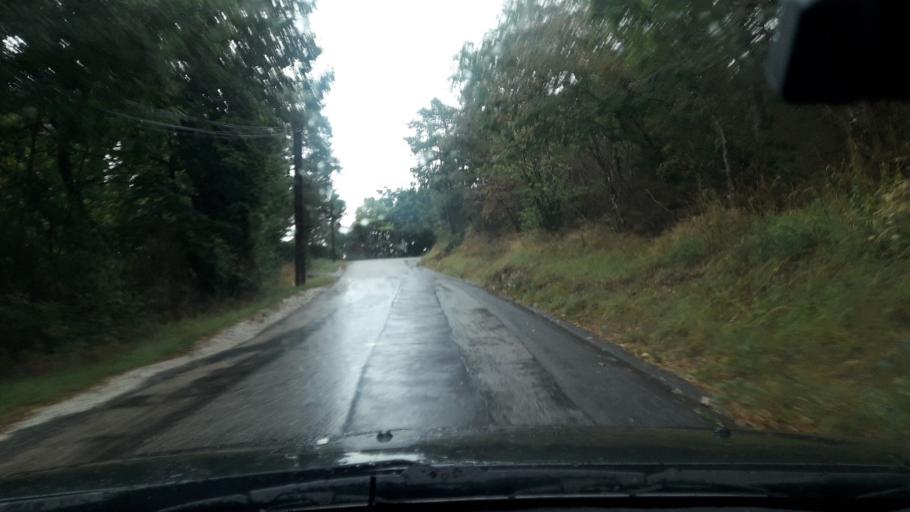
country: FR
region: Rhone-Alpes
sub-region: Departement de la Savoie
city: Saint-Baldoph
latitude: 45.5215
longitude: 5.9366
